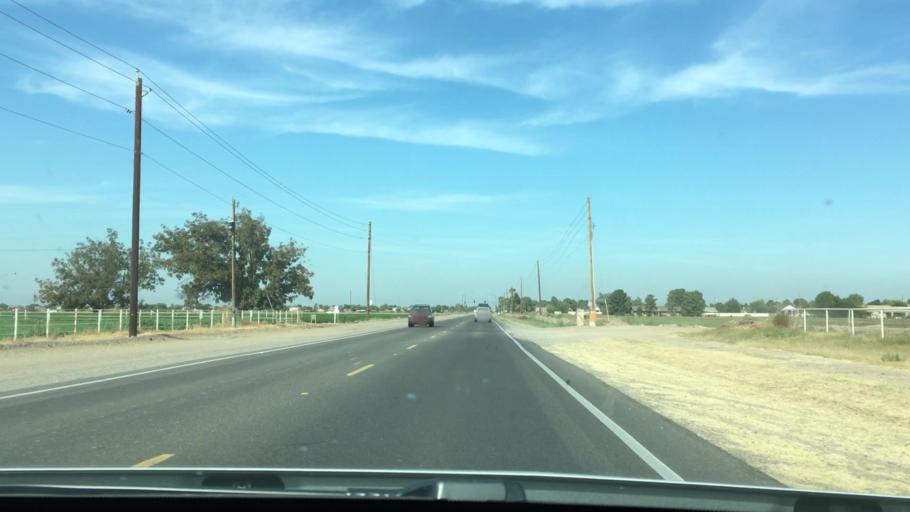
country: US
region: Arizona
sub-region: Maricopa County
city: Chandler
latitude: 33.2443
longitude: -111.7554
